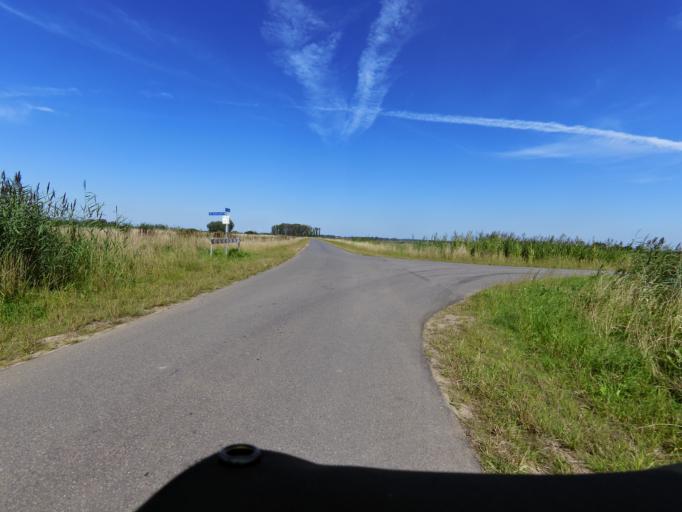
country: NL
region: South Holland
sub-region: Gemeente Hardinxveld-Giessendam
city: Neder-Hardinxveld
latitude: 51.7784
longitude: 4.8368
